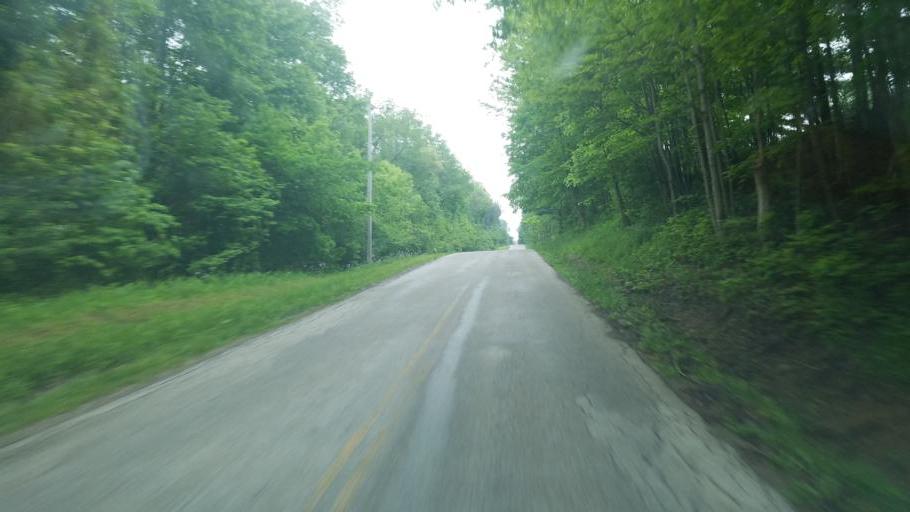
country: US
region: Ohio
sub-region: Sandusky County
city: Bellville
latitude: 40.6578
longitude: -82.4726
